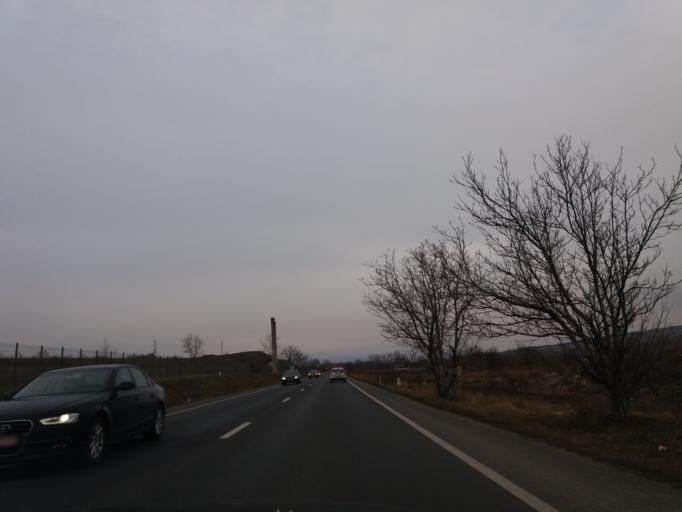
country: RO
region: Hunedoara
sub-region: Comuna Calan
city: Calan
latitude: 45.7448
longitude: 22.9998
